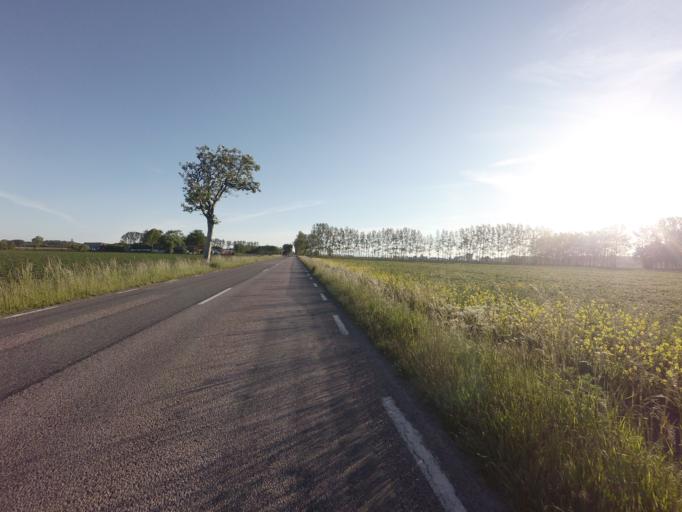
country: SE
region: Skane
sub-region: Hoganas Kommun
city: Hoganas
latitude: 56.2089
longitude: 12.6762
